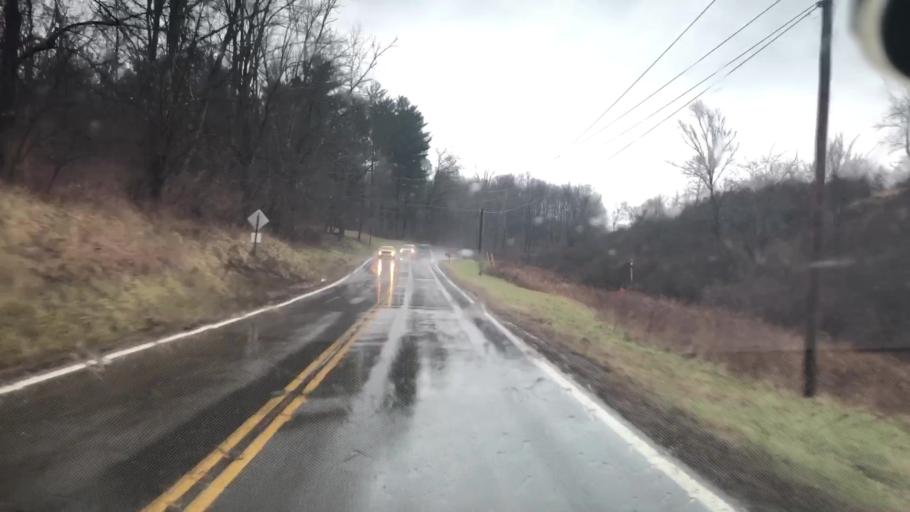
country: US
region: Ohio
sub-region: Harrison County
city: Cadiz
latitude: 40.1667
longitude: -80.9833
